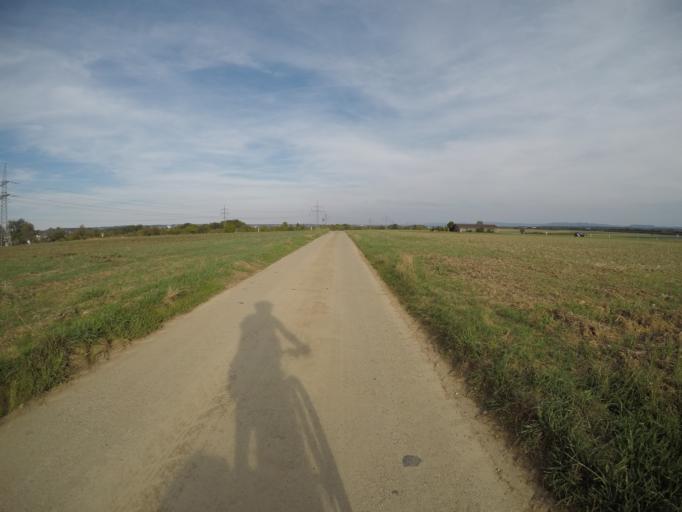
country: DE
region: Baden-Wuerttemberg
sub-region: Regierungsbezirk Stuttgart
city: Neuhausen auf den Fildern
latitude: 48.7018
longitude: 9.2636
